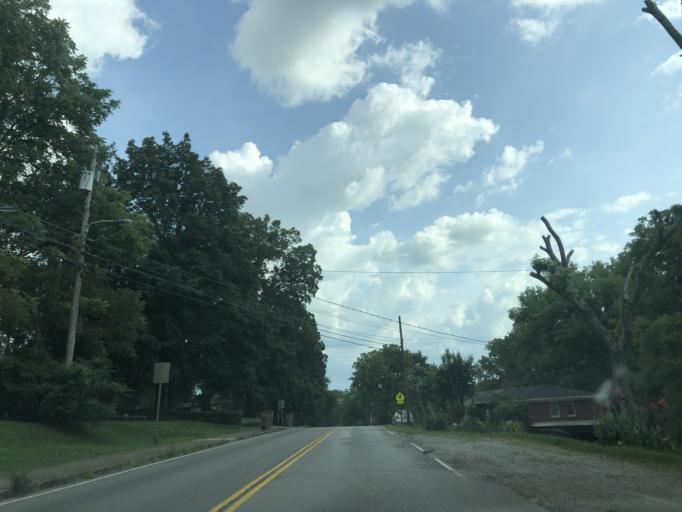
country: US
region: Tennessee
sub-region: Davidson County
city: Lakewood
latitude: 36.1629
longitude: -86.6811
